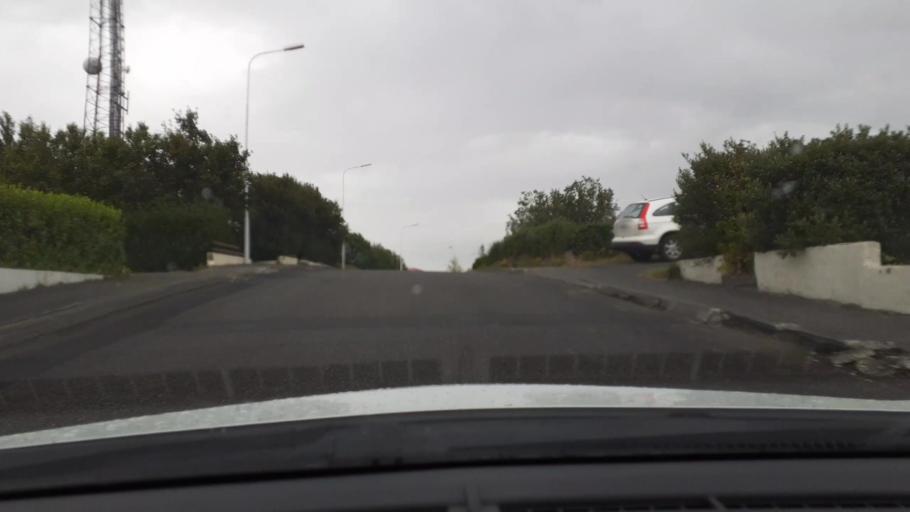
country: IS
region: West
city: Borgarnes
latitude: 64.5386
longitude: -21.9168
